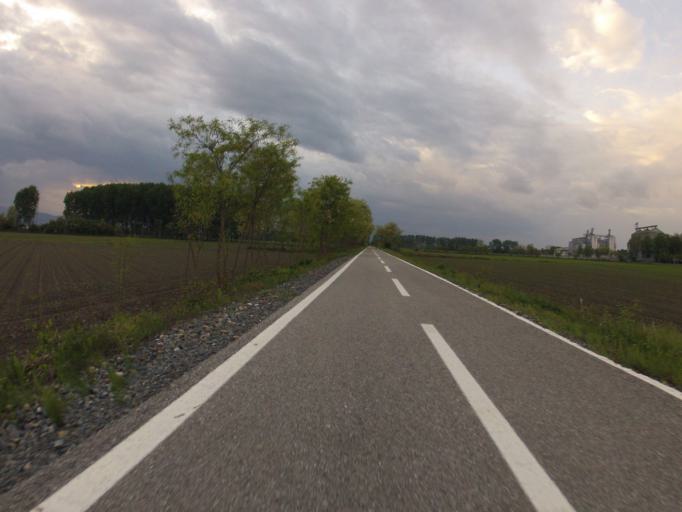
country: IT
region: Piedmont
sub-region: Provincia di Torino
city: Vigone
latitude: 44.8201
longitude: 7.4967
